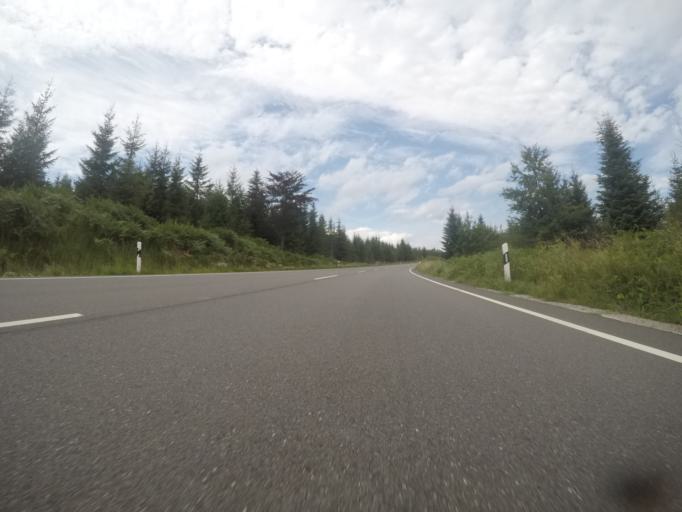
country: DE
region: Baden-Wuerttemberg
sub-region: Freiburg Region
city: Bad Peterstal-Griesbach
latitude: 48.5019
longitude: 8.2267
